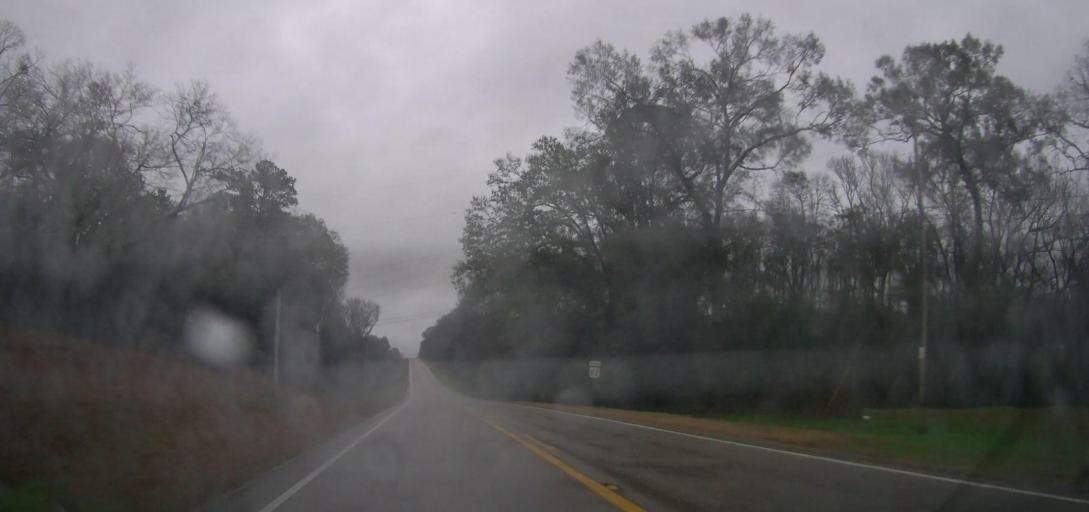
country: US
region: Alabama
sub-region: Autauga County
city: Pine Level
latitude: 32.5332
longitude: -86.6380
